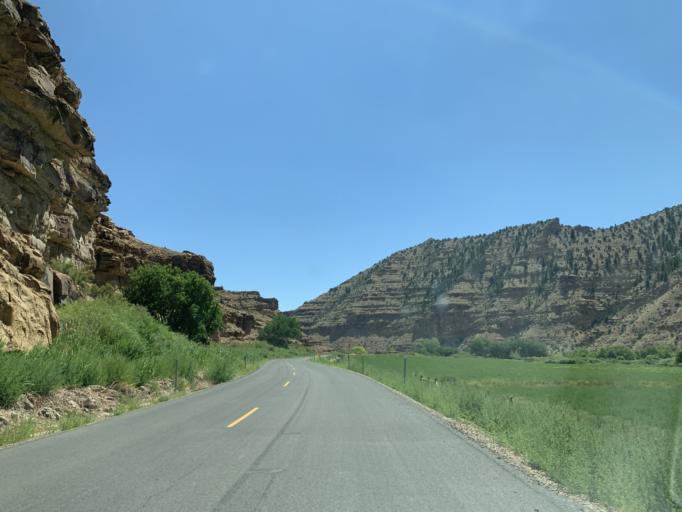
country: US
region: Utah
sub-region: Carbon County
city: East Carbon City
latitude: 39.8090
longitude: -110.2647
